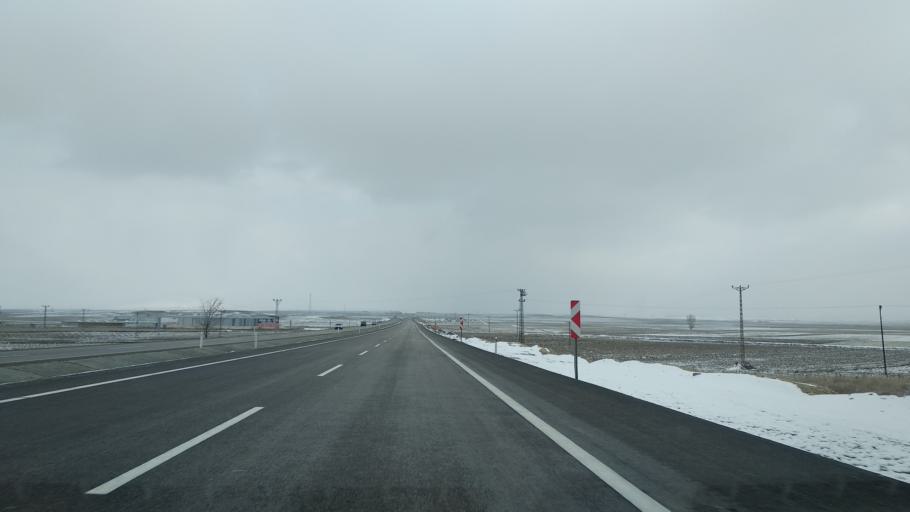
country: TR
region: Kayseri
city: Elbasi
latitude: 38.6539
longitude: 36.0117
